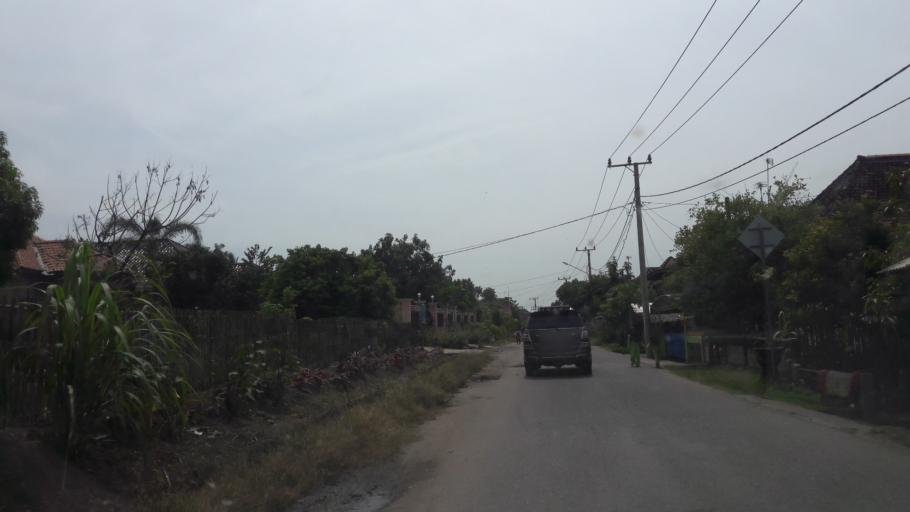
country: ID
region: South Sumatra
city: Gunungmenang
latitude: -3.1835
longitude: 104.1094
